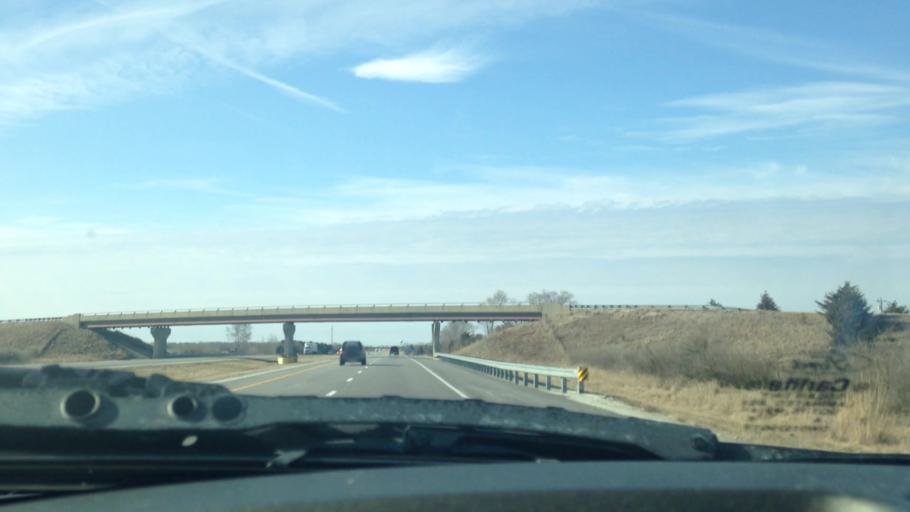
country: US
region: Illinois
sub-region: Ford County
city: Paxton
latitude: 40.4876
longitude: -88.0967
